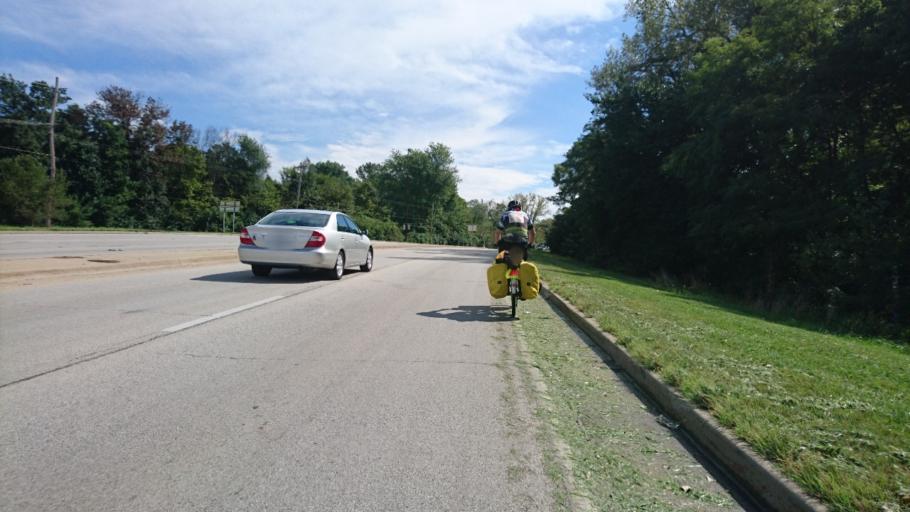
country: US
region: Illinois
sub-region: Sangamon County
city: Grandview
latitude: 39.8451
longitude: -89.6326
